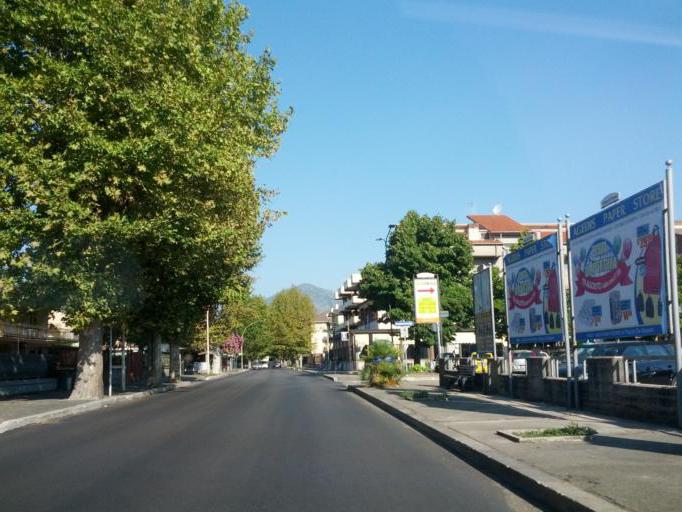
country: IT
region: Latium
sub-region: Provincia di Latina
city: Fondi
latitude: 41.3509
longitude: 13.4375
